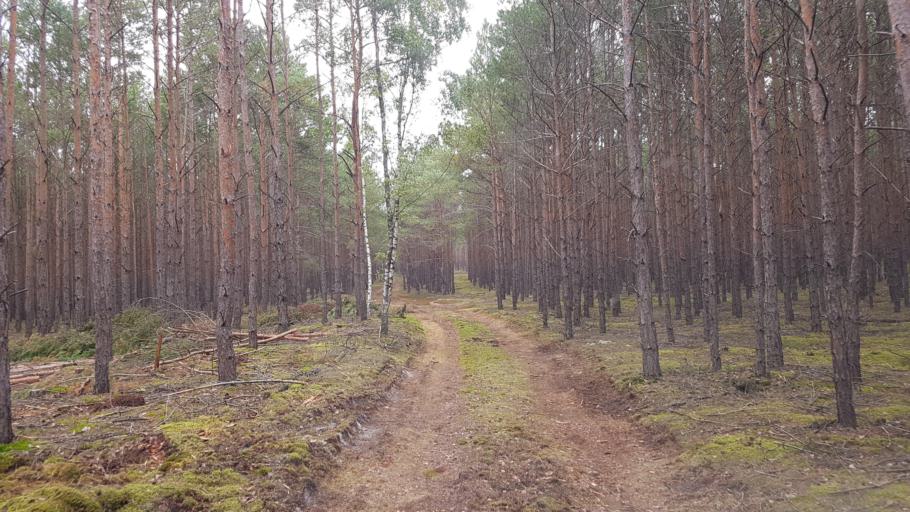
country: DE
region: Brandenburg
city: Doberlug-Kirchhain
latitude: 51.6107
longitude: 13.6217
